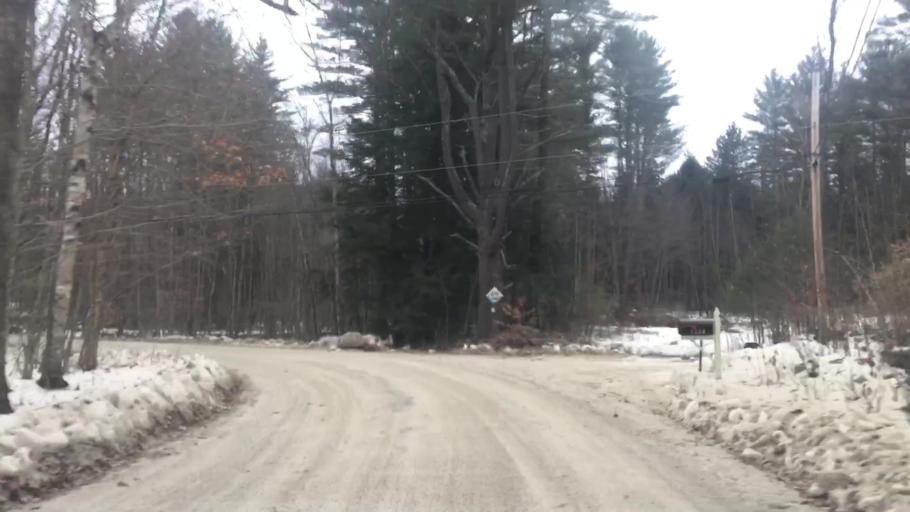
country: US
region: New Hampshire
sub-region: Merrimack County
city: Hopkinton
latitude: 43.1582
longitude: -71.6660
